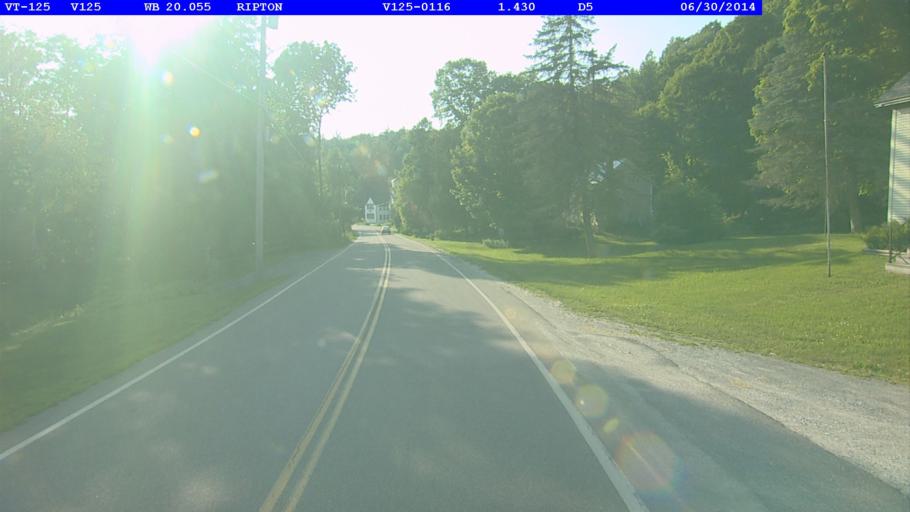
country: US
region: Vermont
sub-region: Addison County
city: Middlebury (village)
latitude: 43.9742
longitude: -73.0344
